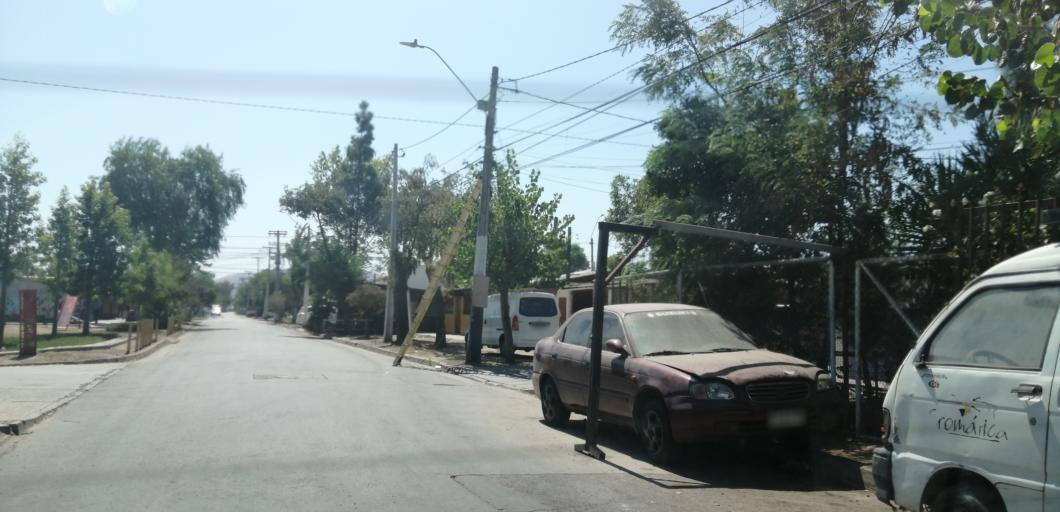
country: CL
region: Santiago Metropolitan
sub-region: Provincia de Santiago
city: Lo Prado
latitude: -33.4347
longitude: -70.7428
